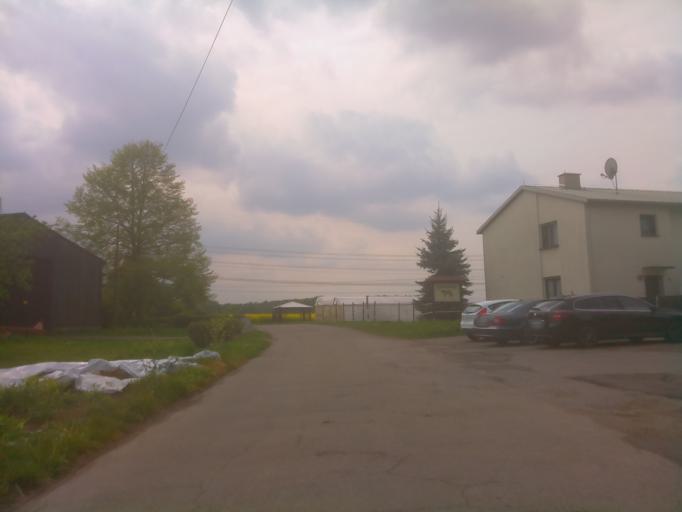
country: DE
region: Baden-Wuerttemberg
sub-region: Karlsruhe Region
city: Edingen-Neckarhausen
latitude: 49.4297
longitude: 8.5780
